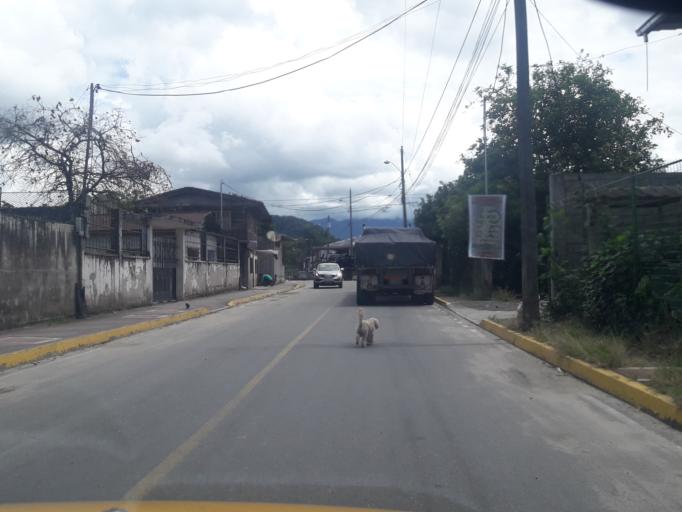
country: EC
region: Napo
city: Tena
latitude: -1.0049
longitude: -77.8195
